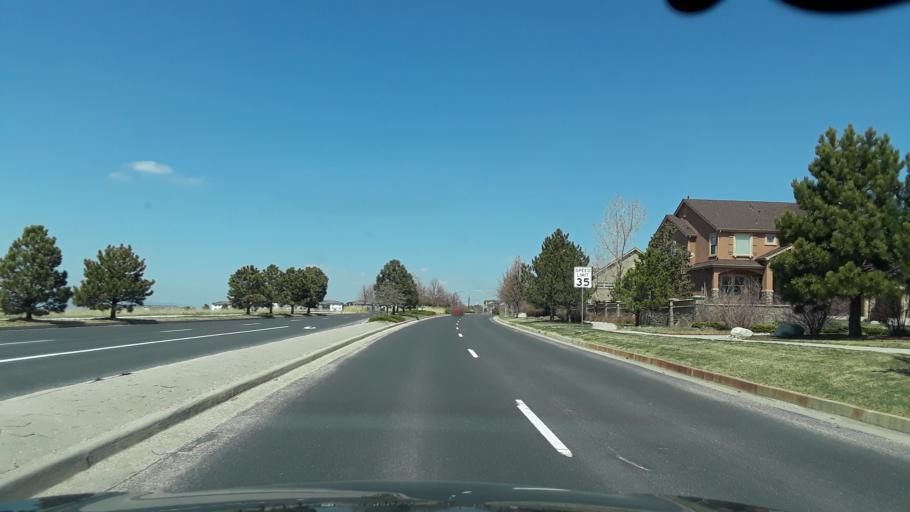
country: US
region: Colorado
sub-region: El Paso County
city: Black Forest
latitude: 38.9683
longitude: -104.7376
